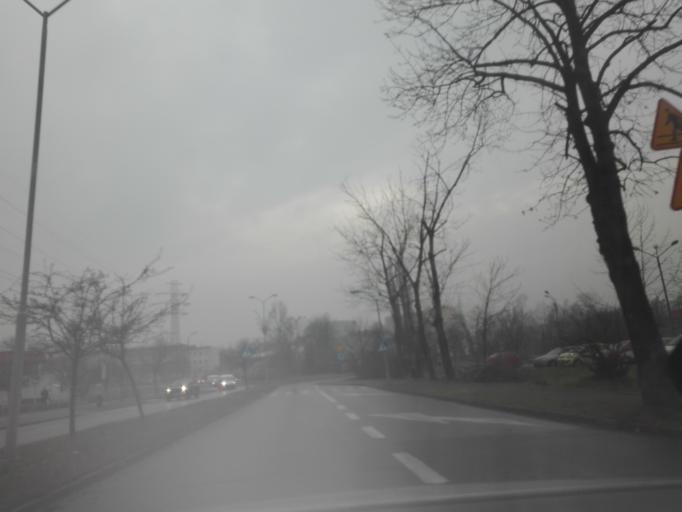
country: PL
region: Silesian Voivodeship
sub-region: Chorzow
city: Chorzow
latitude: 50.2609
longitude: 18.9702
